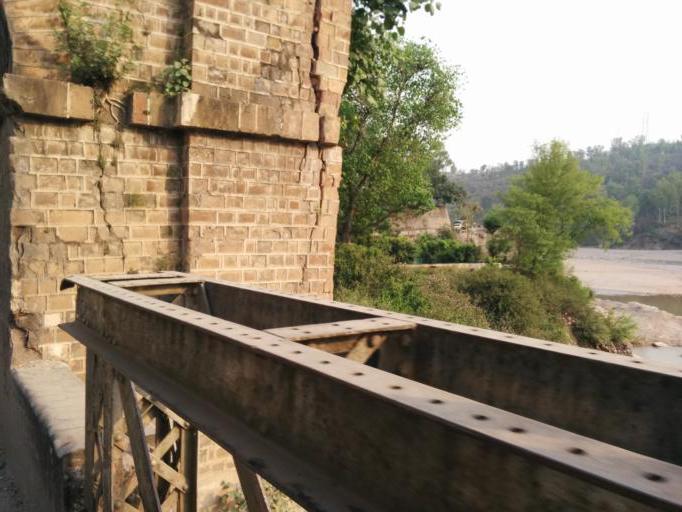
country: IN
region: Himachal Pradesh
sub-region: Kangra
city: Kotla
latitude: 32.2373
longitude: 76.0475
